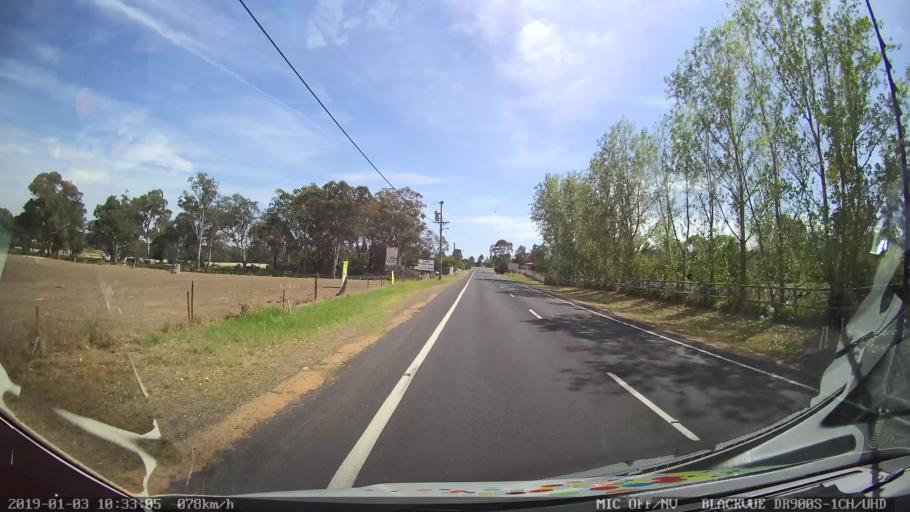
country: AU
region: New South Wales
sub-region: Young
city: Young
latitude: -34.3319
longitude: 148.2855
